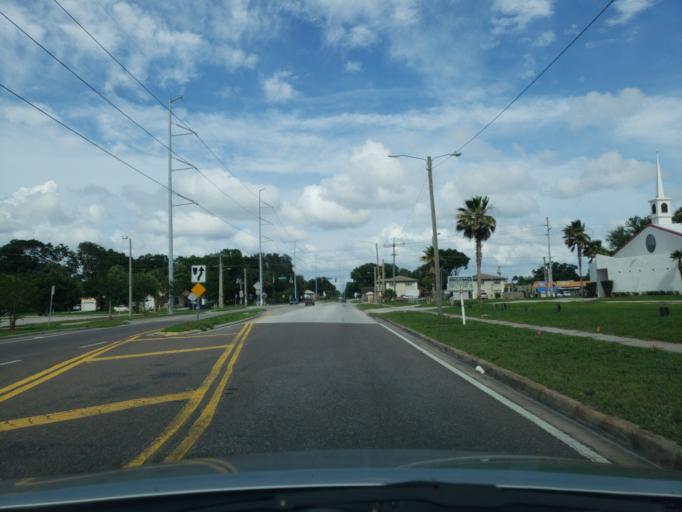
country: US
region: Florida
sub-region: Hillsborough County
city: Egypt Lake-Leto
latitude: 28.0108
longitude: -82.5186
